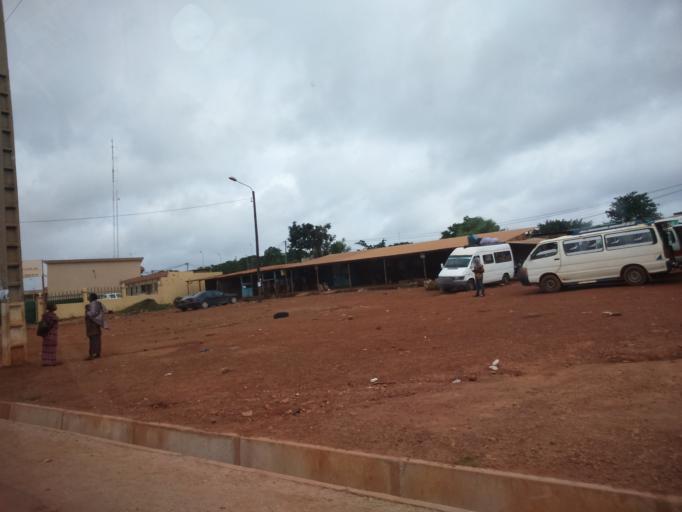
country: CI
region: Moyen-Comoe
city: Abengourou
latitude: 6.7239
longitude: -3.5073
